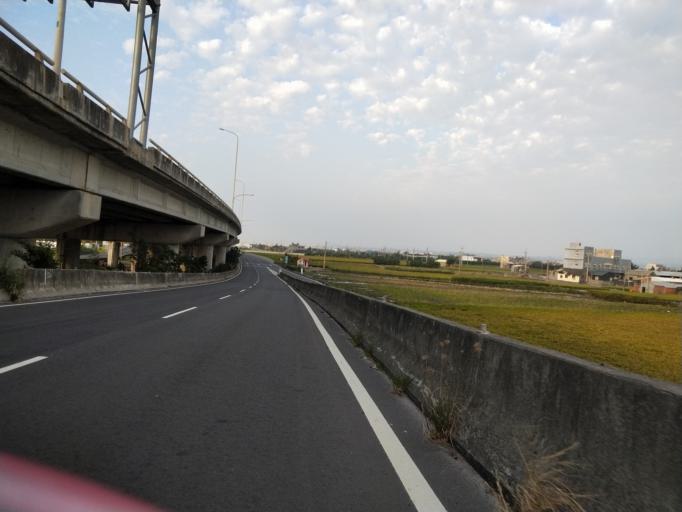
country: TW
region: Taiwan
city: Fengyuan
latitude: 24.4043
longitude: 120.6131
